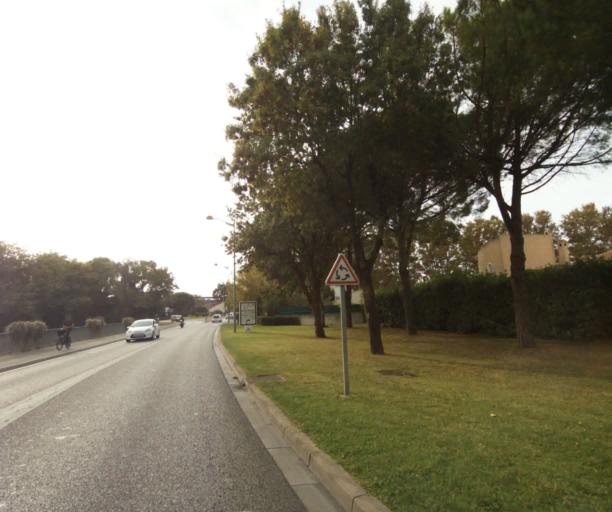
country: FR
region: Provence-Alpes-Cote d'Azur
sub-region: Departement des Bouches-du-Rhone
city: Marignane
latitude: 43.4112
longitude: 5.2122
